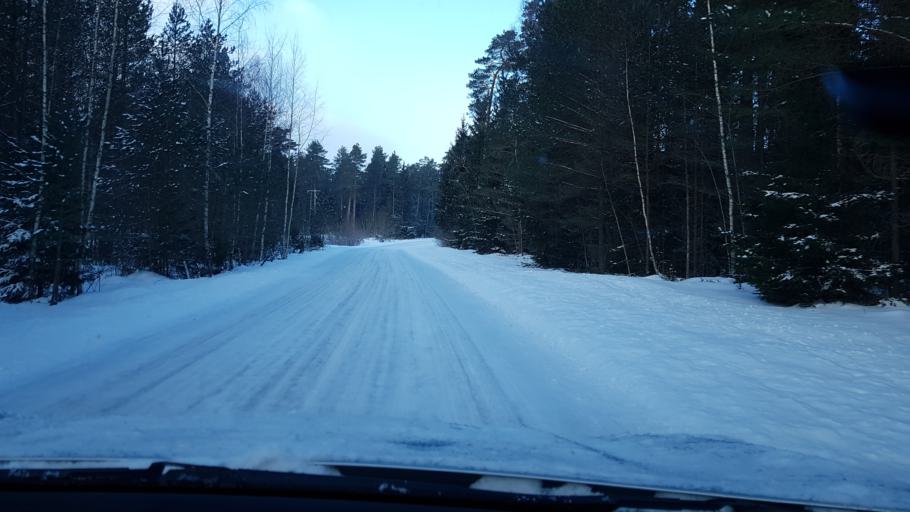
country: EE
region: Harju
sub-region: Nissi vald
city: Turba
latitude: 59.2171
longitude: 24.1404
